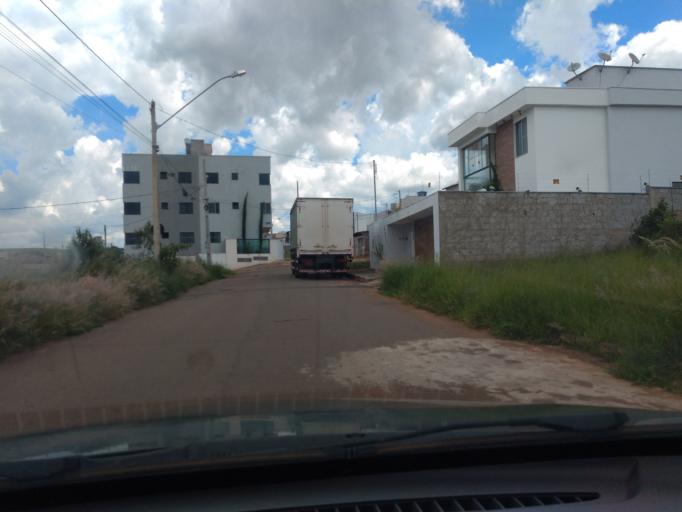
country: BR
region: Minas Gerais
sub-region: Tres Coracoes
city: Tres Coracoes
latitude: -21.6811
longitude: -45.2645
